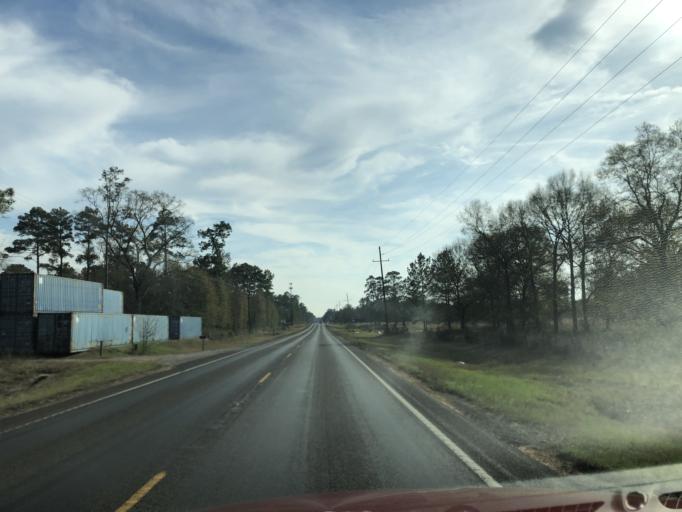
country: US
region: Texas
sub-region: Montgomery County
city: Magnolia
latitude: 30.2770
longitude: -95.8329
